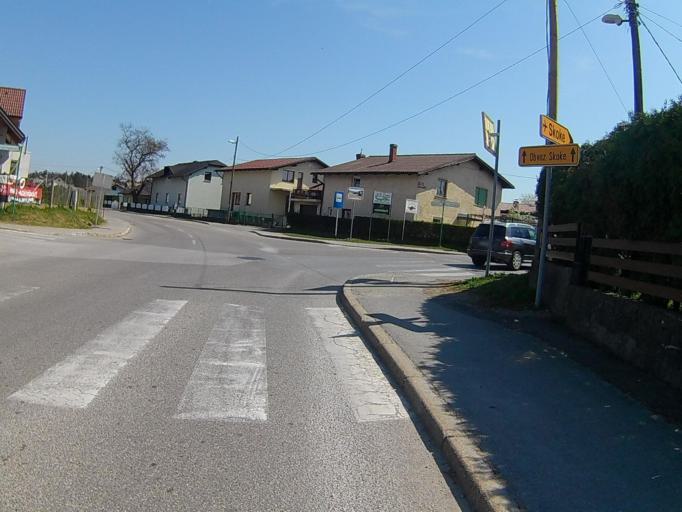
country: SI
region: Hoce-Slivnica
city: Rogoza
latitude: 46.4998
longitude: 15.6803
